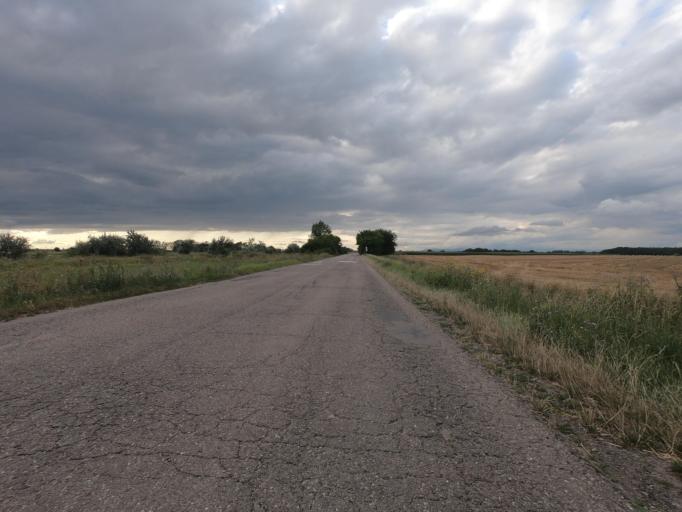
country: HU
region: Heves
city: Poroszlo
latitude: 47.6755
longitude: 20.6569
